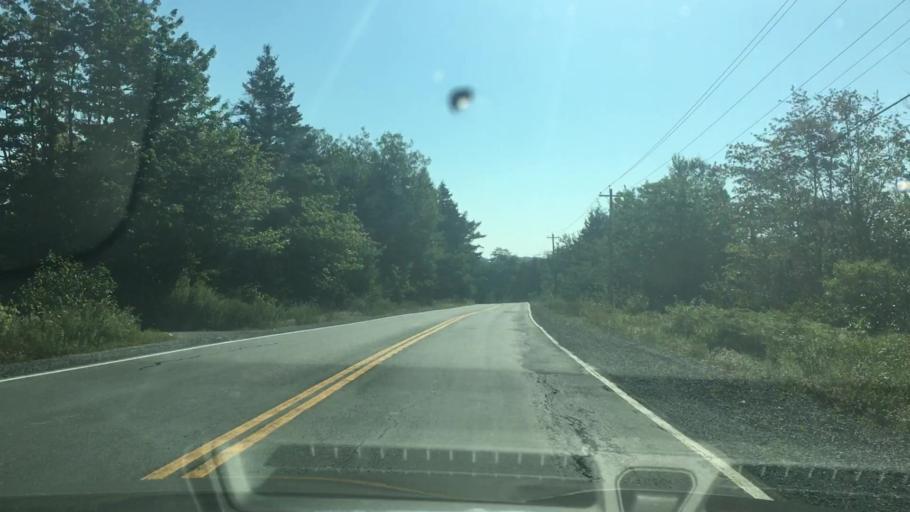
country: CA
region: Nova Scotia
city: Cole Harbour
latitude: 44.7776
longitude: -63.0739
